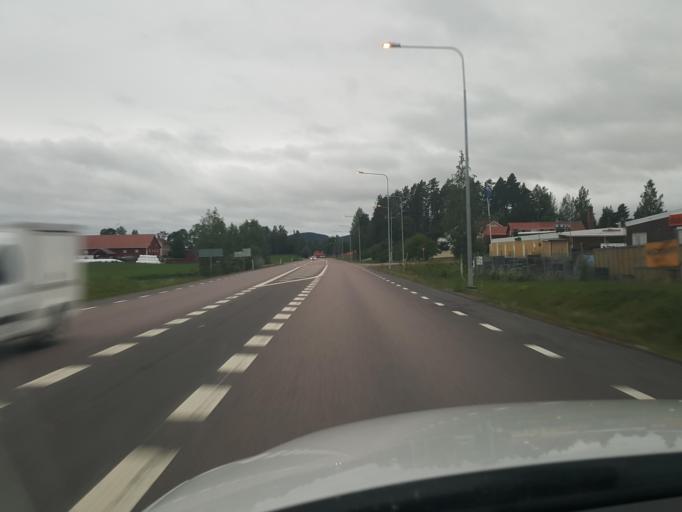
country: SE
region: Gaevleborg
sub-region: Bollnas Kommun
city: Bollnas
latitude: 61.3553
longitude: 16.4264
